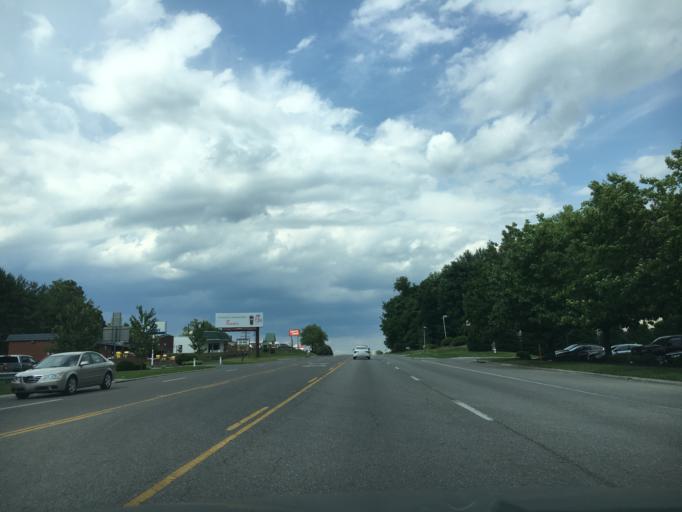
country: US
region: Virginia
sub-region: Roanoke County
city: Cave Spring
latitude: 37.2250
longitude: -80.0124
